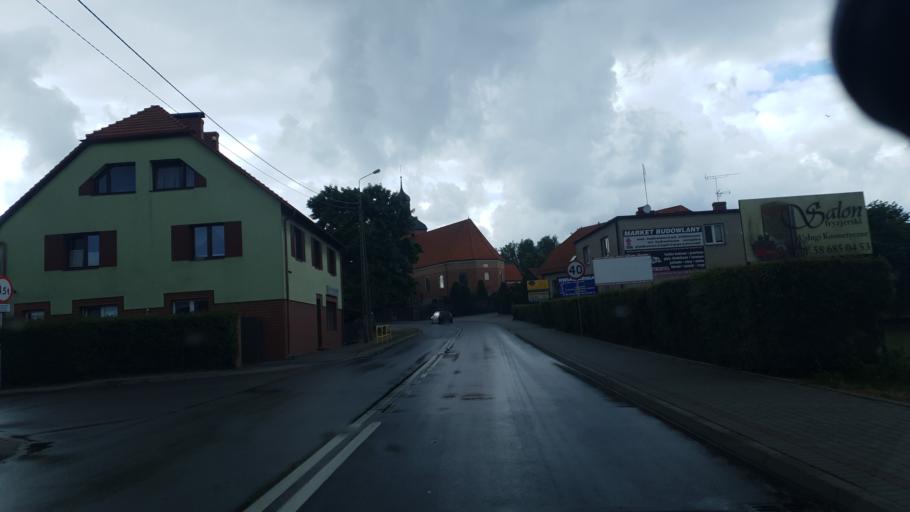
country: PL
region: Pomeranian Voivodeship
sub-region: Powiat kartuski
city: Stezyca
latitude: 54.2067
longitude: 17.9537
